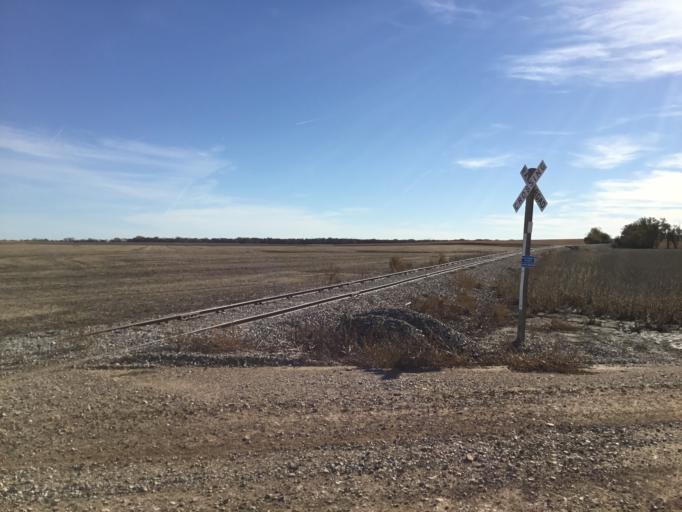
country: US
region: Kansas
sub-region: Lincoln County
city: Lincoln
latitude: 38.9962
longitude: -98.0774
